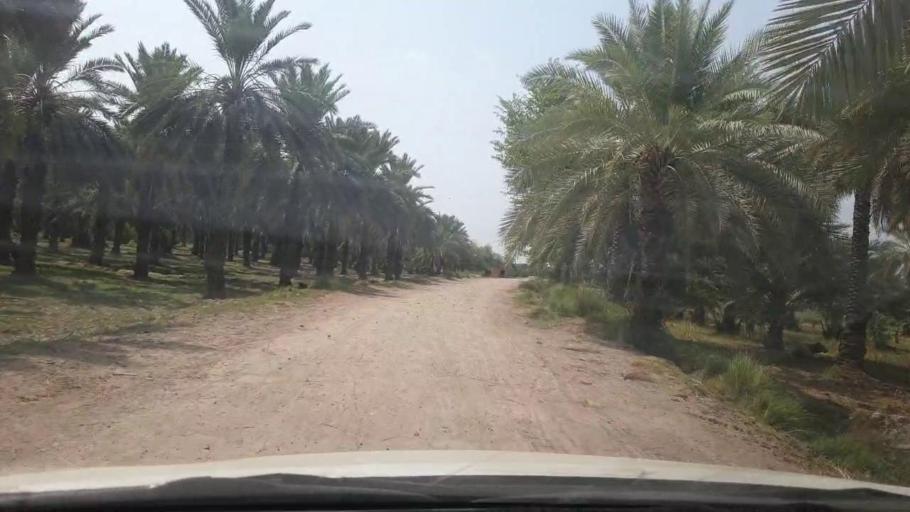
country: PK
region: Sindh
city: Khairpur
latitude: 27.5619
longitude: 68.8472
